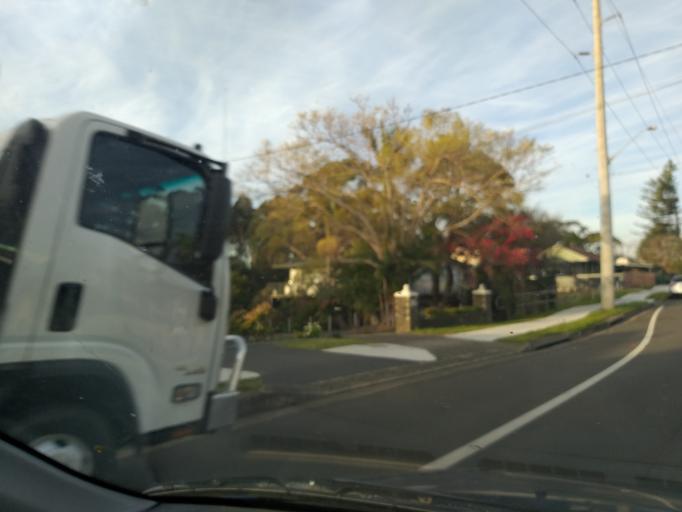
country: AU
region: New South Wales
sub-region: Wollongong
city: Corrimal
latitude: -34.3820
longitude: 150.8889
